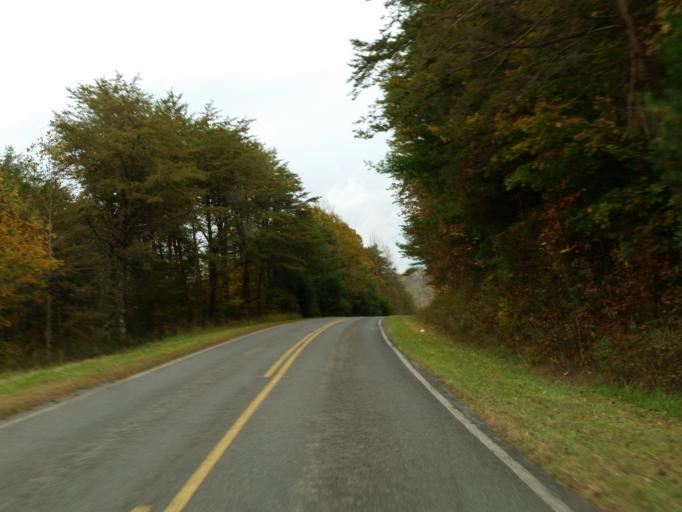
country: US
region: Georgia
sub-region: Fannin County
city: Blue Ridge
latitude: 34.6751
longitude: -84.2756
